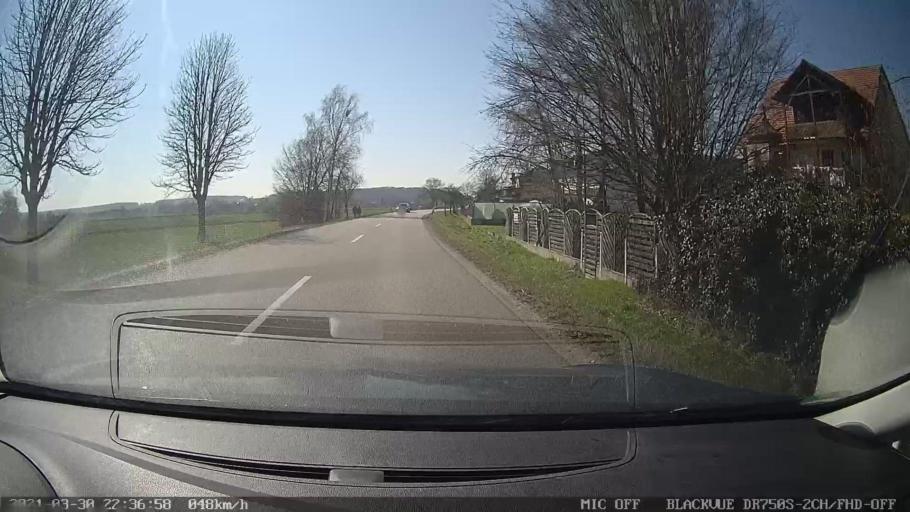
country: DE
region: Bavaria
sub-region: Upper Palatinate
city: Zeitlarn
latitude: 49.0906
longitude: 12.1097
